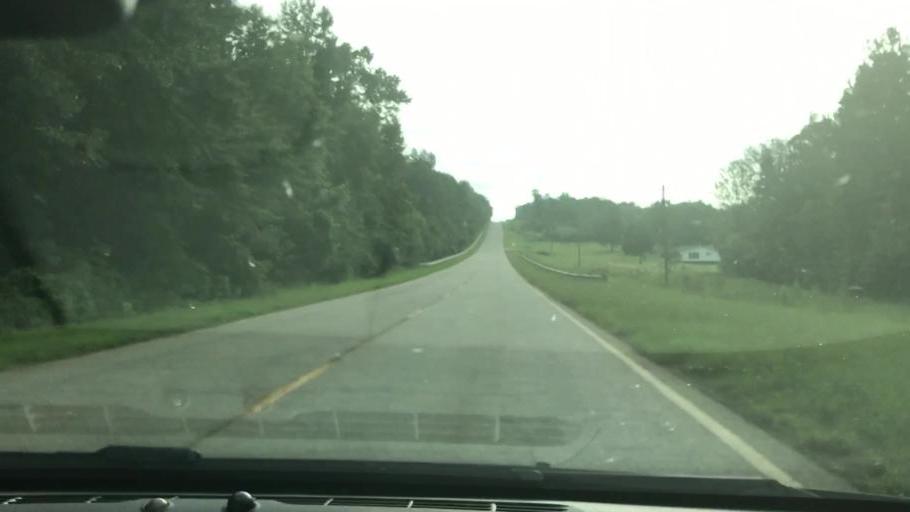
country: US
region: Georgia
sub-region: Quitman County
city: Georgetown
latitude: 31.8934
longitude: -85.0724
